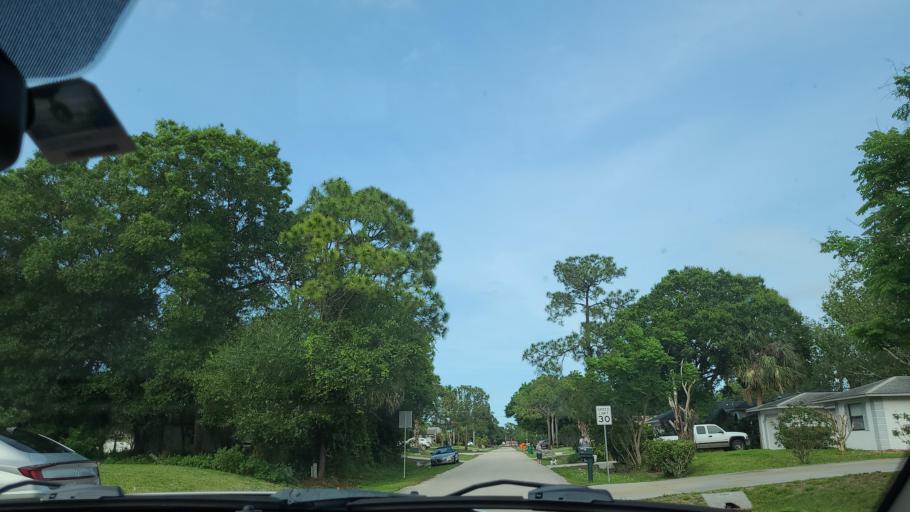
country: US
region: Florida
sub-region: Indian River County
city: Sebastian
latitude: 27.7738
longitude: -80.4912
